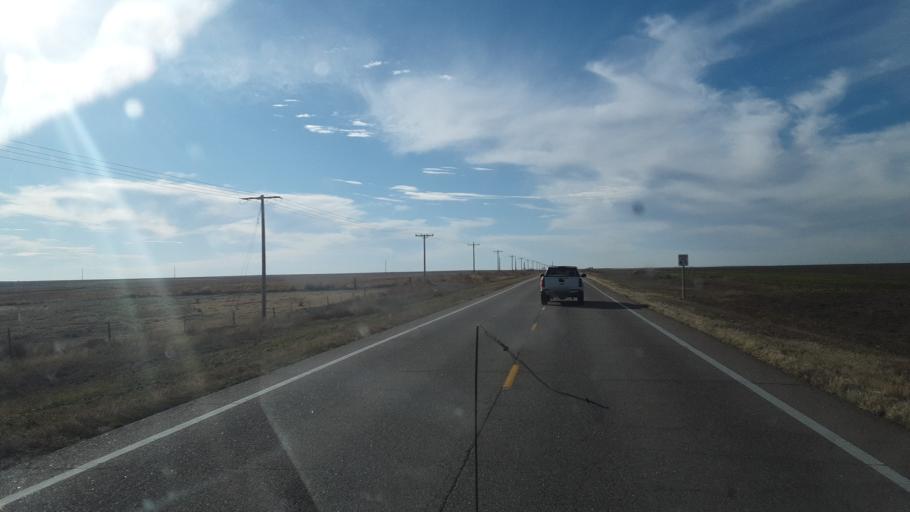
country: US
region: Kansas
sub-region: Finney County
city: Garden City
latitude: 38.0601
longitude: -100.6119
